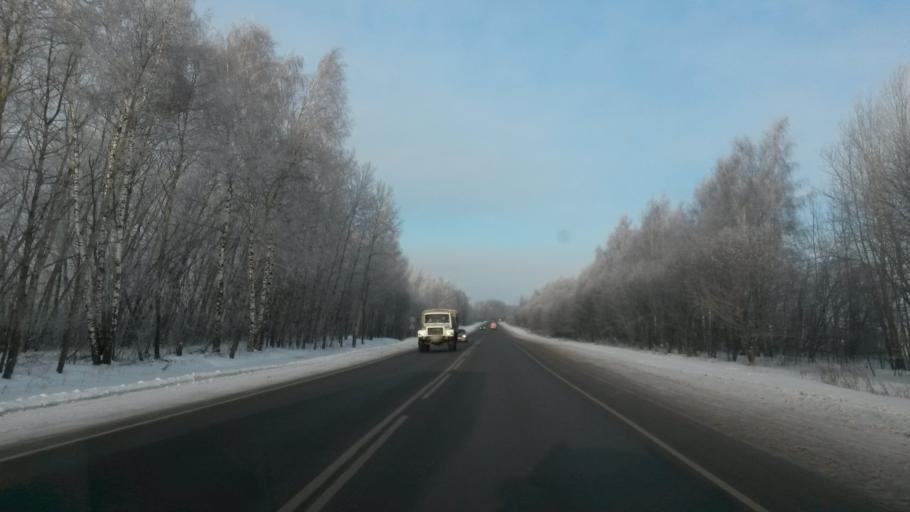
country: RU
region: Vladimir
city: Bogolyubovo
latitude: 56.2045
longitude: 40.4440
